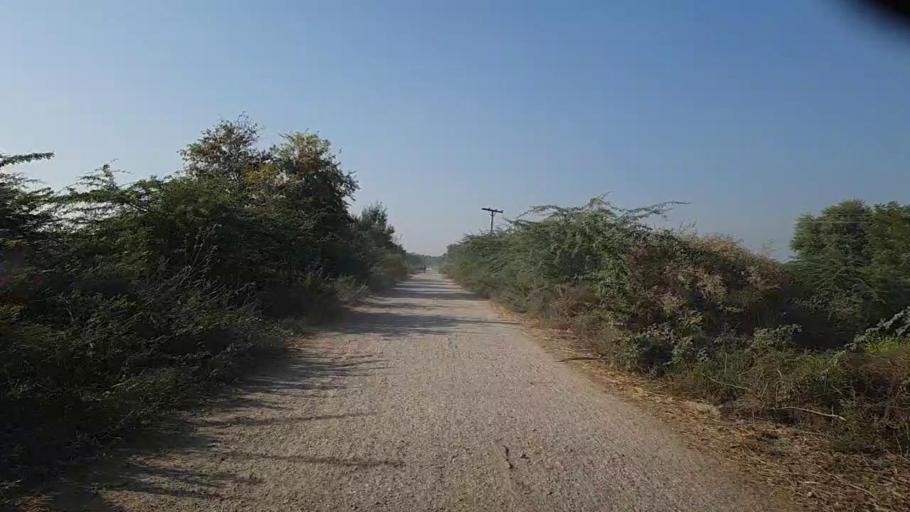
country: PK
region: Sindh
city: Darya Khan Marri
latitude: 26.6764
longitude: 68.3758
